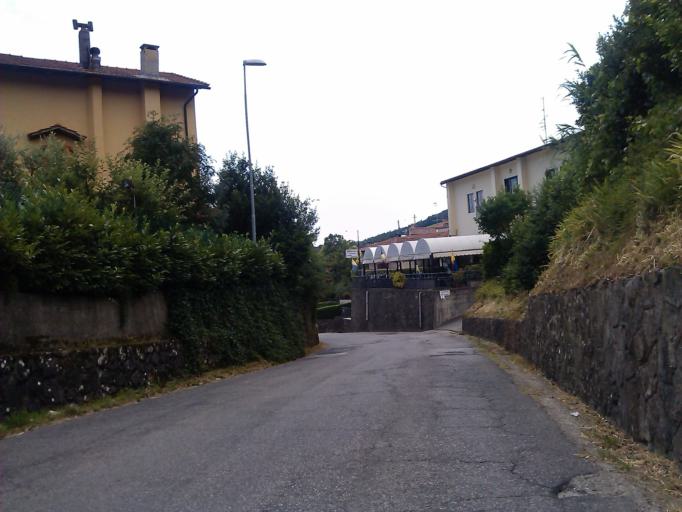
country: IT
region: Tuscany
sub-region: Provincia di Prato
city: Montemurlo
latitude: 43.9553
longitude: 11.0388
